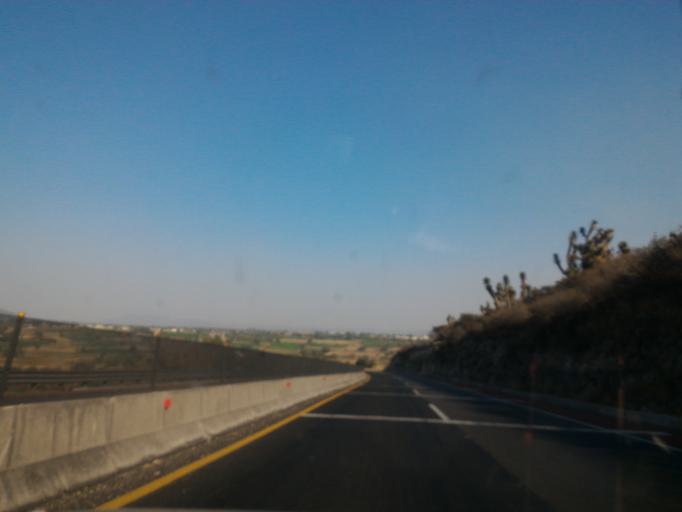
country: MX
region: Hidalgo
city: San Marcos
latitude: 20.0745
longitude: -99.3558
